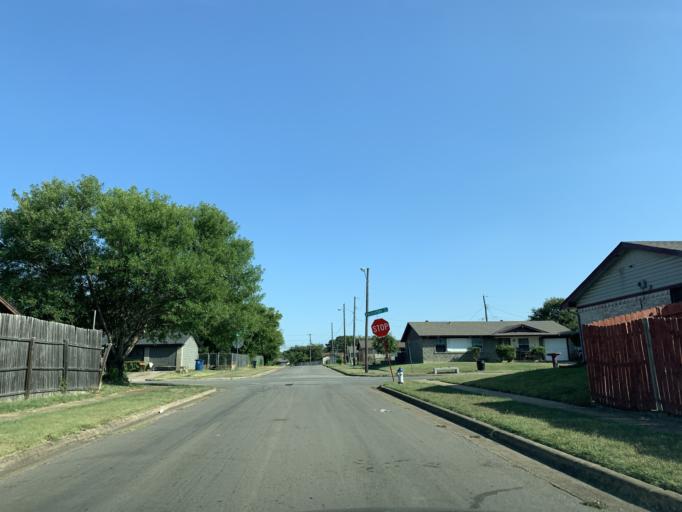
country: US
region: Texas
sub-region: Dallas County
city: Hutchins
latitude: 32.6672
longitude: -96.7637
